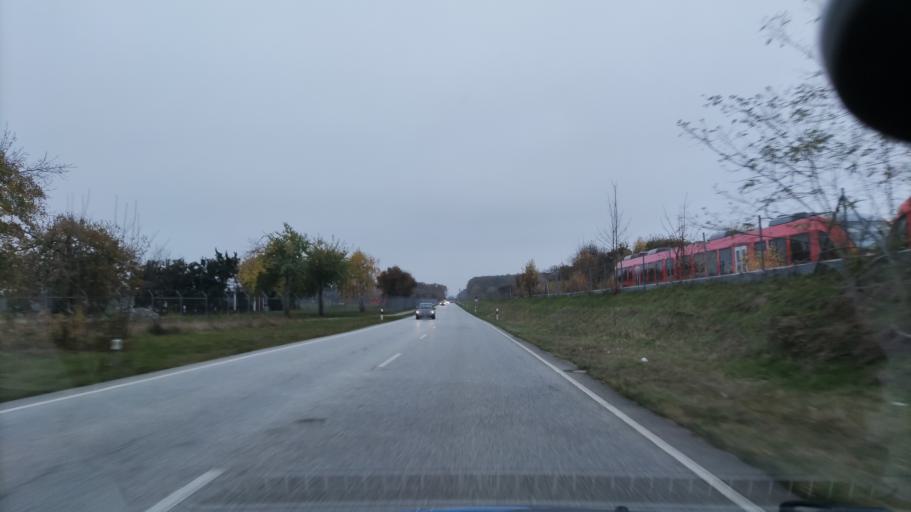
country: DE
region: Schleswig-Holstein
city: Klempau
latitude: 53.8038
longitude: 10.6983
